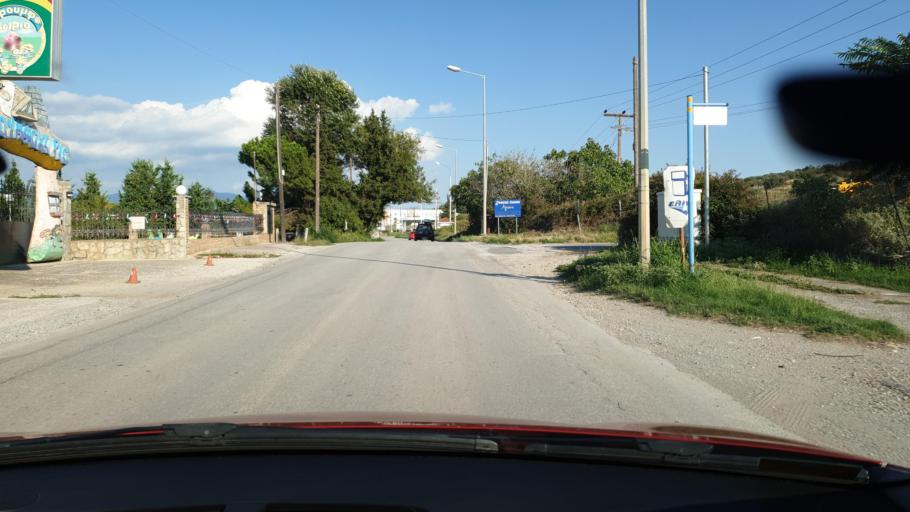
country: GR
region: Central Macedonia
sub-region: Nomos Thessalonikis
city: Neo Rysi
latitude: 40.4951
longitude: 23.0066
